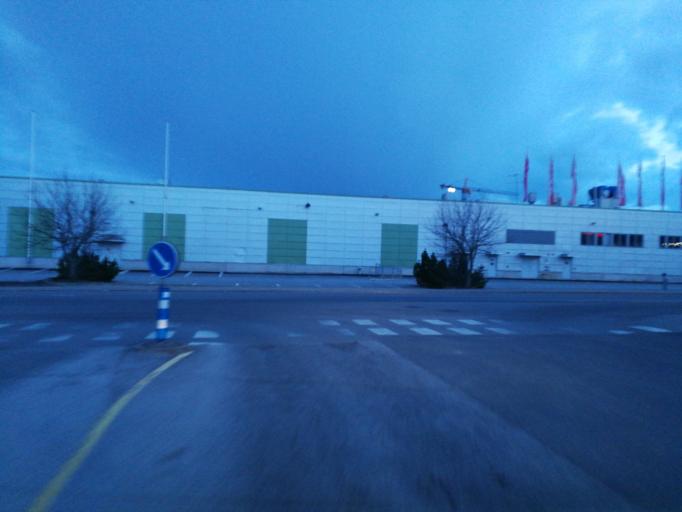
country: FI
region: Varsinais-Suomi
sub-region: Turku
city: Turku
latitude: 60.4732
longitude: 22.2251
